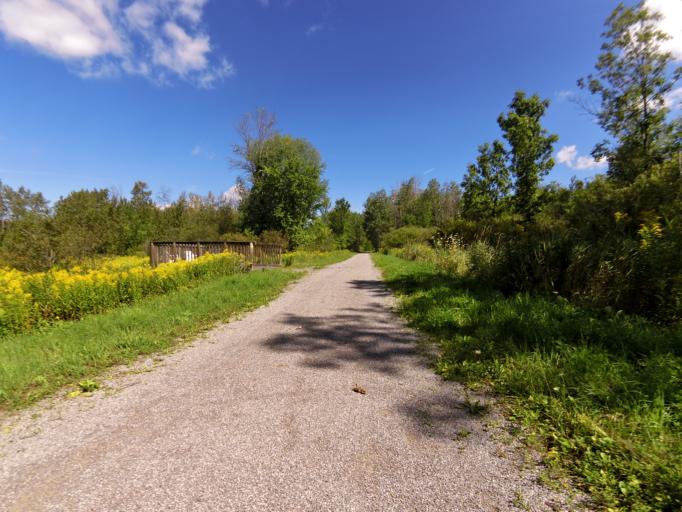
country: CA
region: Ontario
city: Ottawa
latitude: 45.2109
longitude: -75.6249
